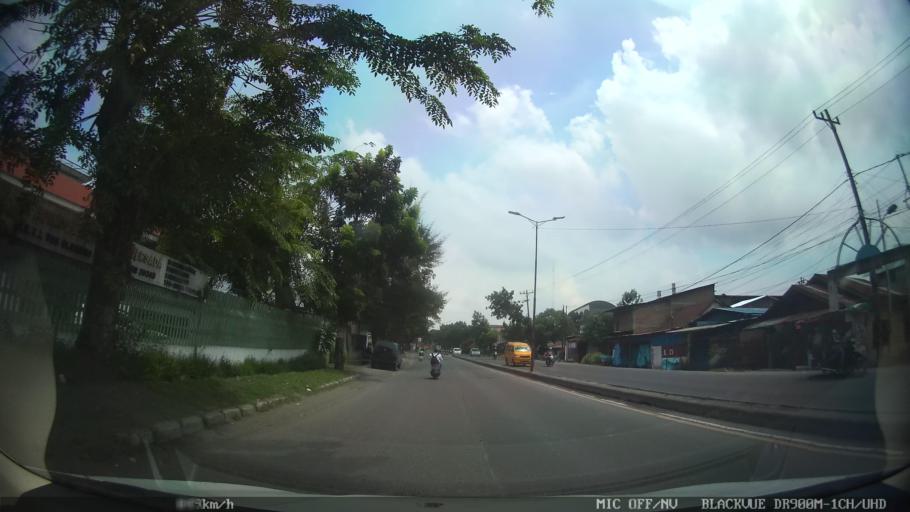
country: ID
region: North Sumatra
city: Labuhan Deli
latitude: 3.6724
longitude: 98.6665
